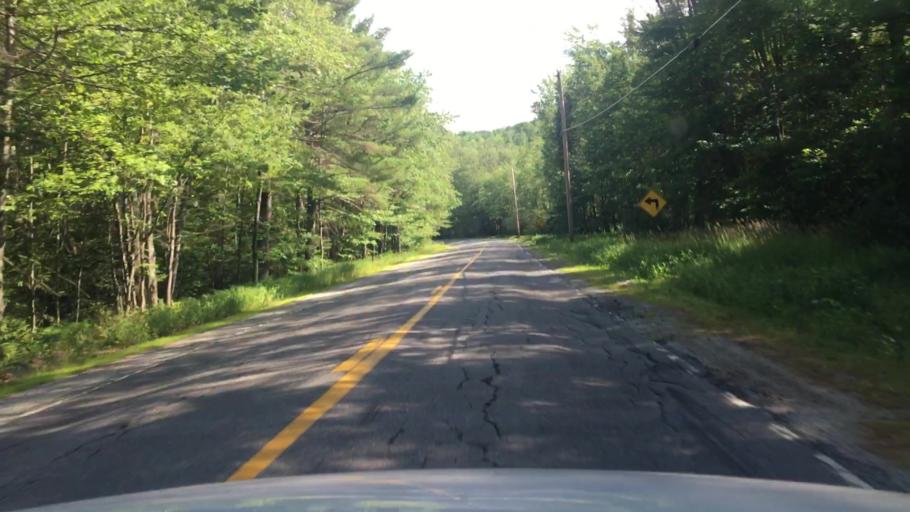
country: US
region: Maine
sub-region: Oxford County
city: Bethel
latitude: 44.3698
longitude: -70.8002
